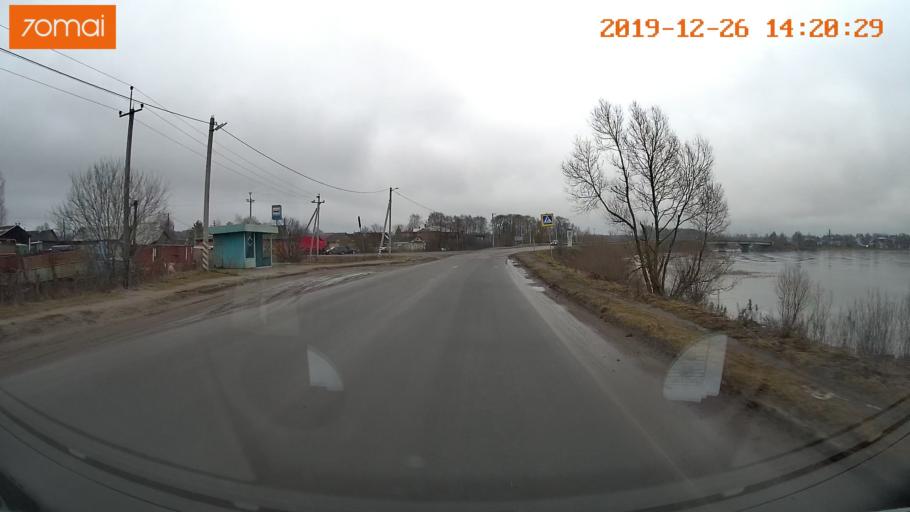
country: RU
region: Jaroslavl
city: Poshekhon'ye
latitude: 58.5096
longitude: 39.1306
